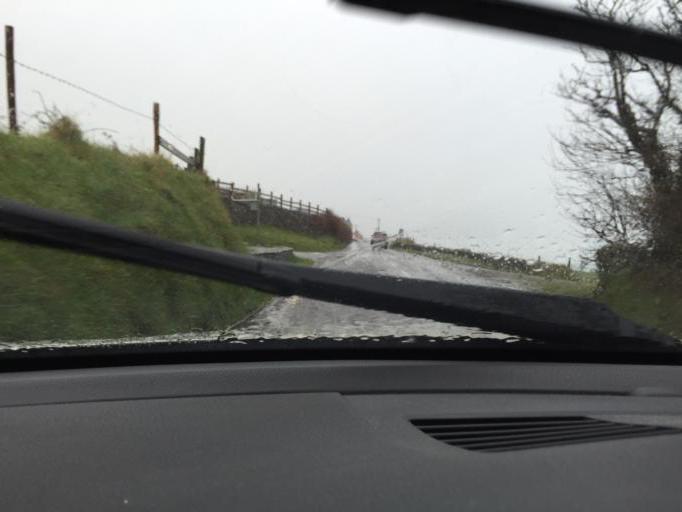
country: IE
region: Munster
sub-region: Ciarrai
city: Dingle
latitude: 52.1340
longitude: -10.3632
